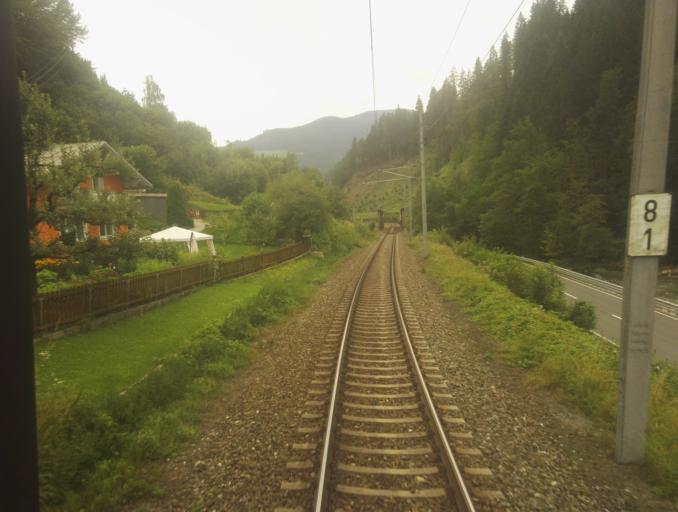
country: AT
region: Salzburg
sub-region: Politischer Bezirk Sankt Johann im Pongau
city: Huttau
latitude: 47.4209
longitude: 13.2990
